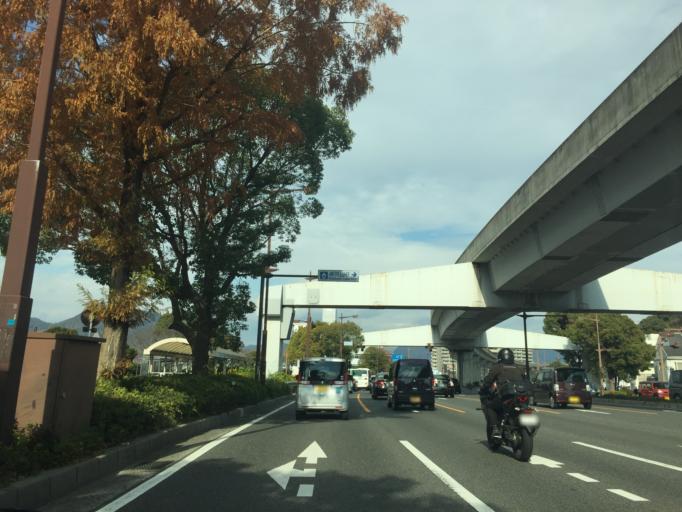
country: JP
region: Hiroshima
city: Hiroshima-shi
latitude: 34.4204
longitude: 132.4651
